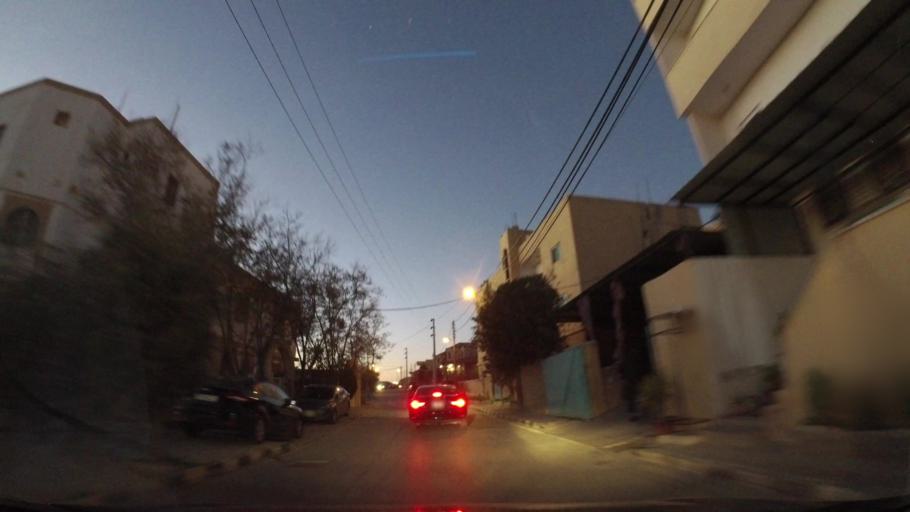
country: JO
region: Ma'an
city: Petra
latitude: 30.3272
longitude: 35.4709
